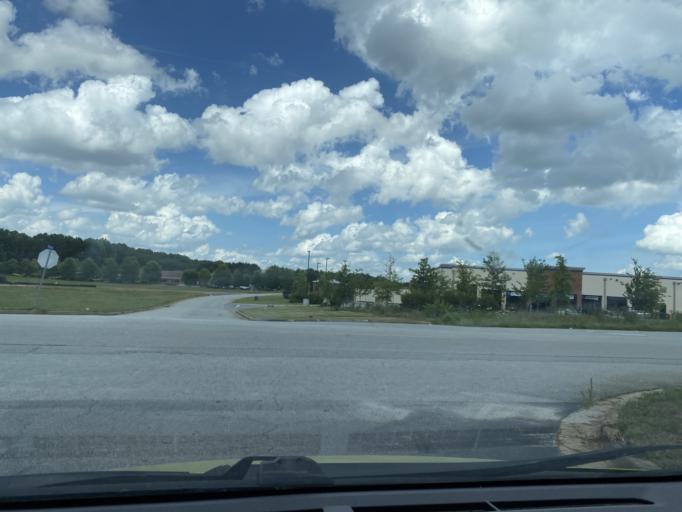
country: US
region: Georgia
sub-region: Fayette County
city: Peachtree City
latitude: 33.4090
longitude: -84.6918
